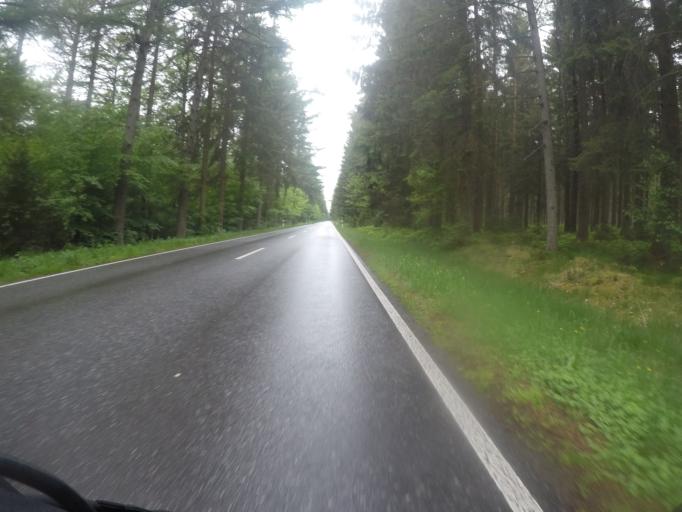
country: DE
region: Schleswig-Holstein
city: Hartenholm
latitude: 53.9229
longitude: 10.0909
